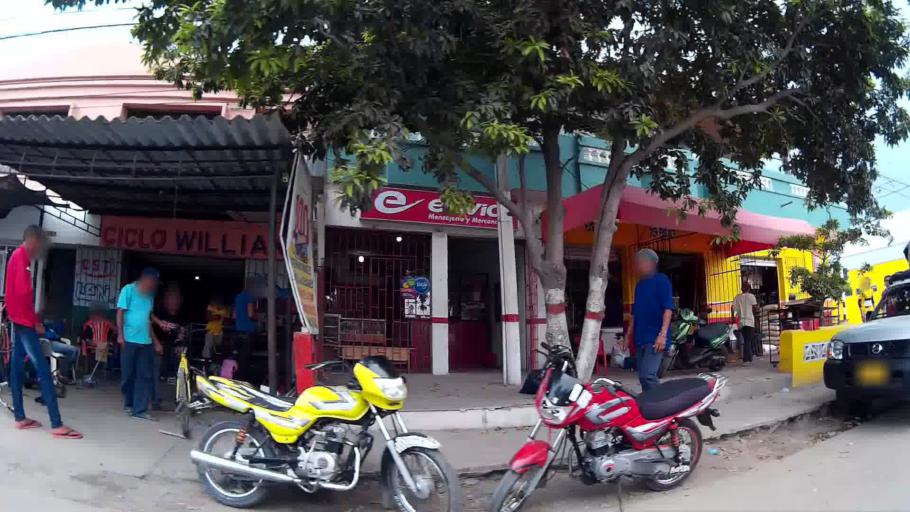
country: CO
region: Magdalena
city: Cienaga
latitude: 11.0063
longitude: -74.2440
